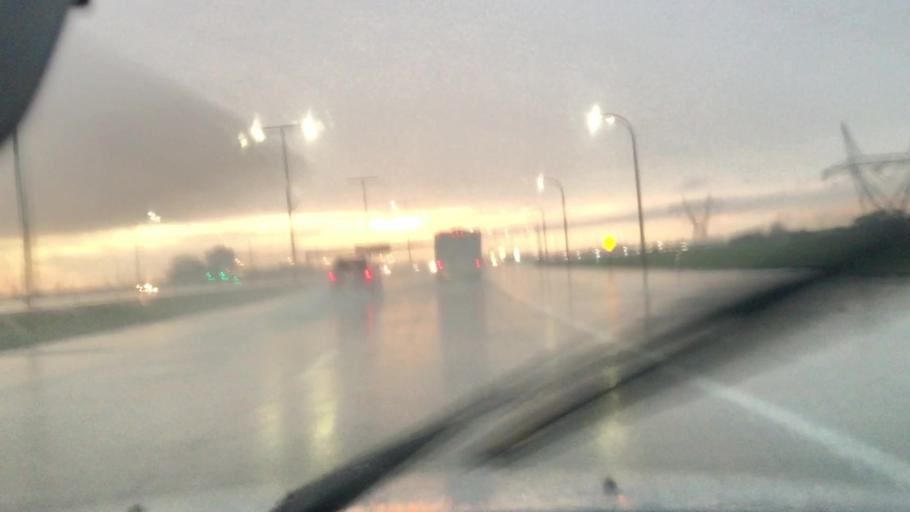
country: CA
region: Alberta
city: Devon
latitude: 53.4313
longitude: -113.5842
